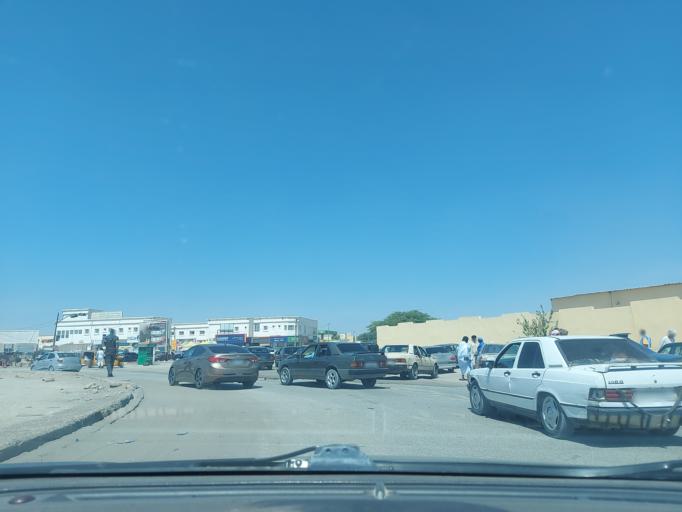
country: MR
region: Nouakchott
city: Nouakchott
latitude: 18.0795
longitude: -15.9652
